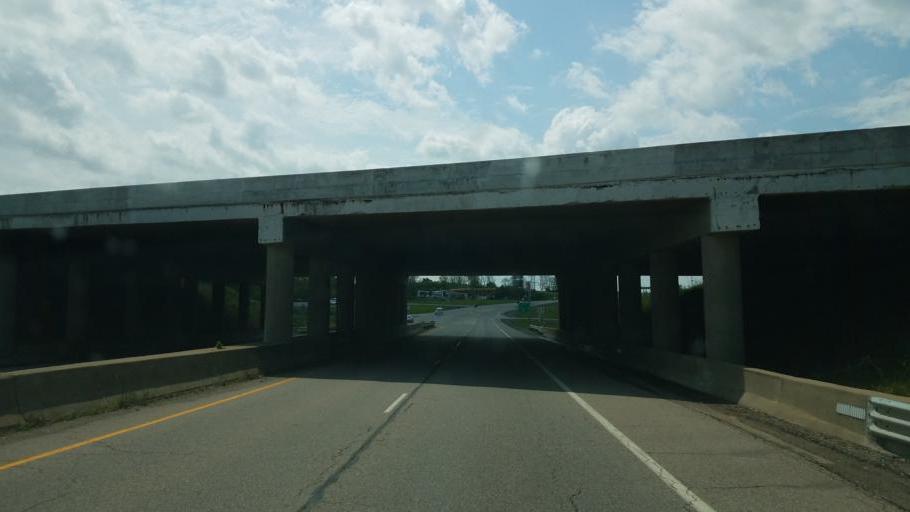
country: US
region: Ohio
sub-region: Licking County
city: Harbor Hills
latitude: 39.9442
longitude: -82.4087
